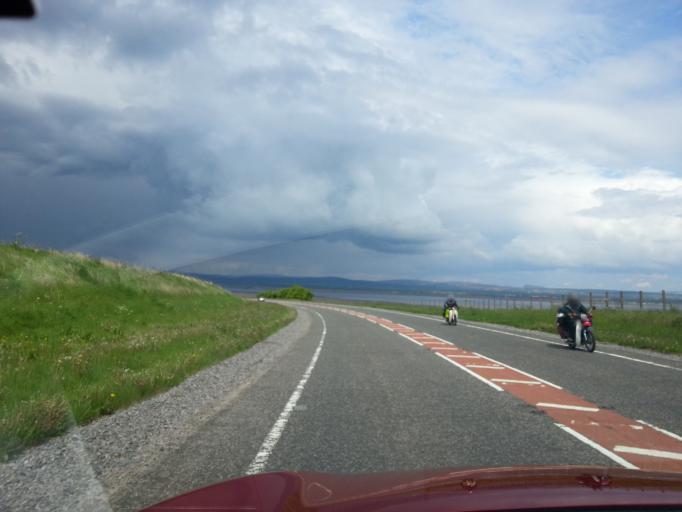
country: GB
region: Scotland
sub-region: Highland
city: Tain
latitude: 57.8265
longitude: -4.0804
